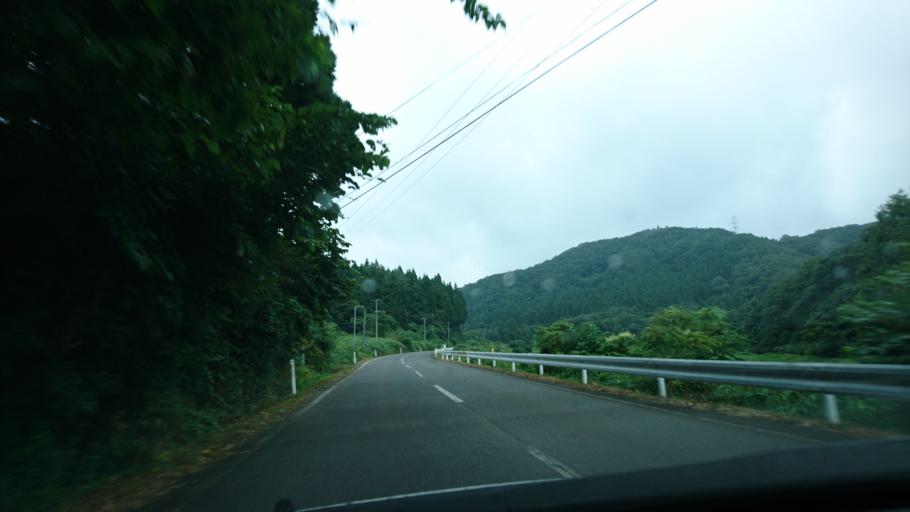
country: JP
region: Iwate
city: Ichinoseki
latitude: 38.8885
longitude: 140.9842
